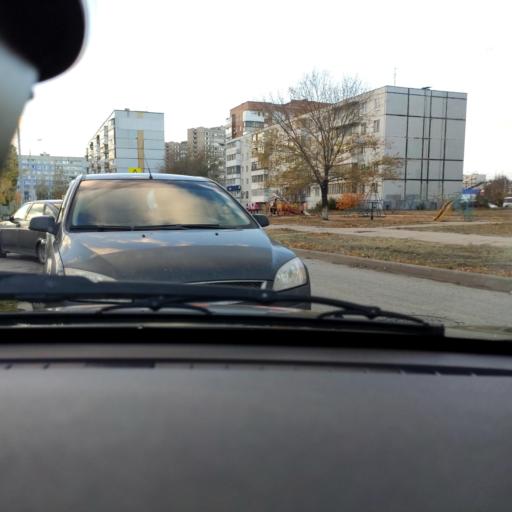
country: RU
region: Samara
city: Zhigulevsk
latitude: 53.4749
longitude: 49.5259
